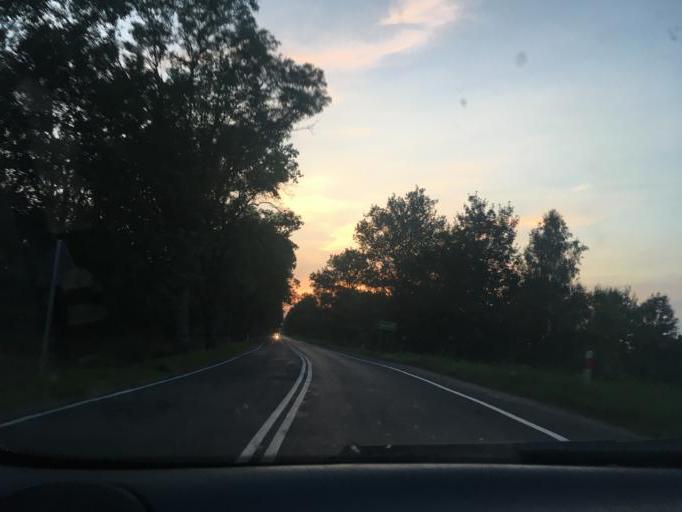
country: PL
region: Lower Silesian Voivodeship
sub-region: Powiat walbrzyski
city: Czarny Bor
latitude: 50.7816
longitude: 16.1012
